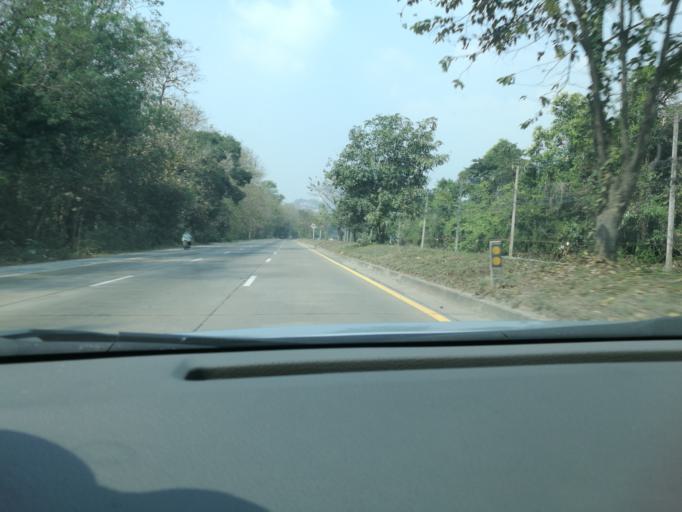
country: TH
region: Sara Buri
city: Chaloem Phra Kiat
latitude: 14.6789
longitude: 100.8781
